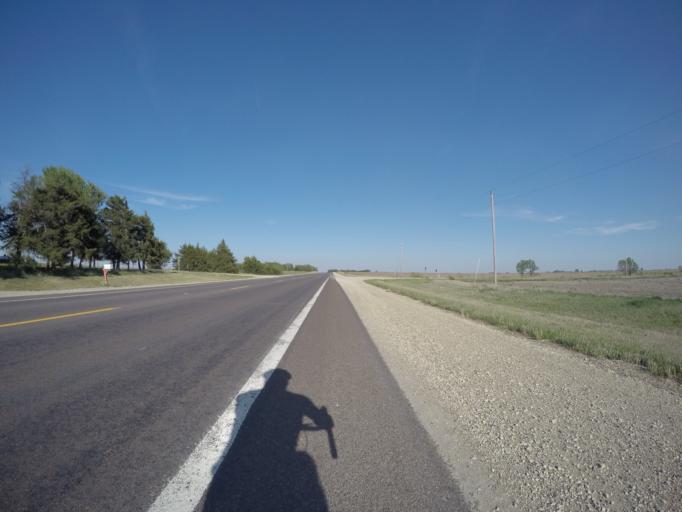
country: US
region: Kansas
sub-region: Riley County
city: Fort Riley North
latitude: 39.2986
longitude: -96.7942
